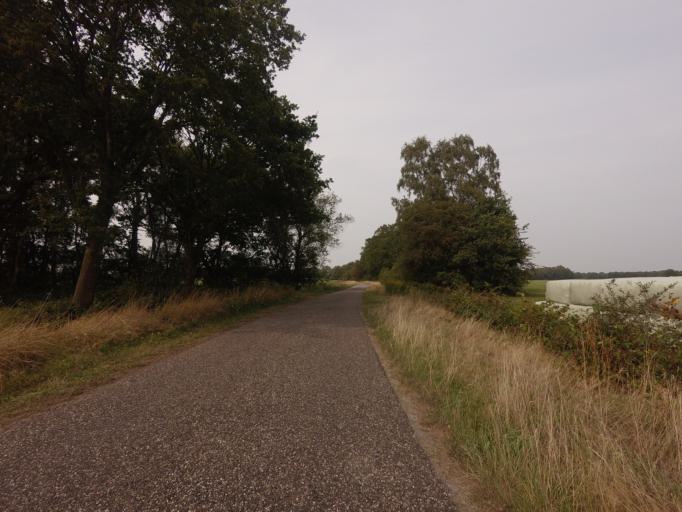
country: NL
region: Drenthe
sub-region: Gemeente Tynaarlo
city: Vries
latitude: 53.1114
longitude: 6.5426
